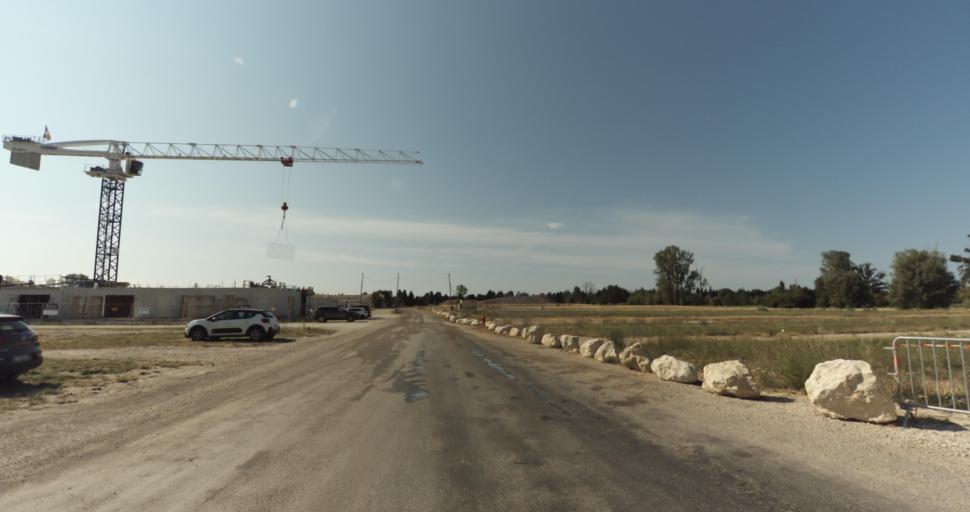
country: FR
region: Provence-Alpes-Cote d'Azur
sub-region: Departement du Vaucluse
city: Althen-des-Paluds
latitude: 44.0171
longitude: 4.9691
